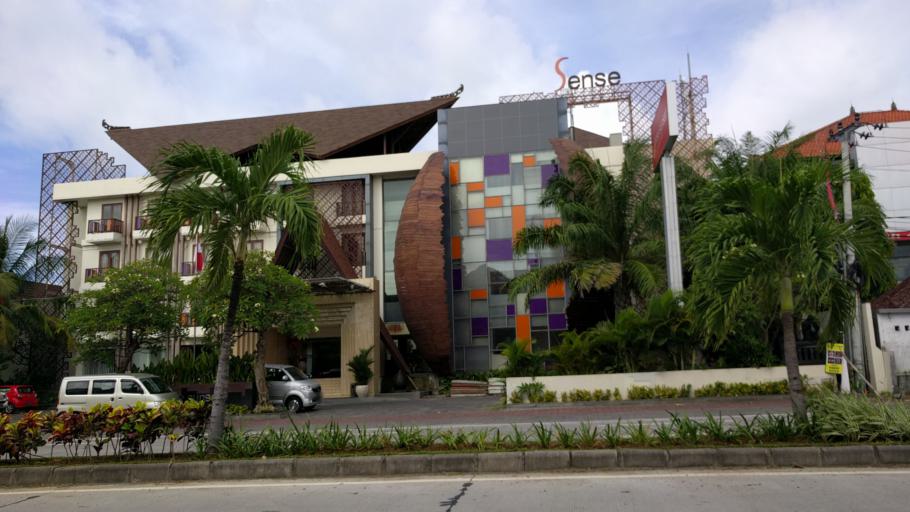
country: ID
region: Bali
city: Kuta
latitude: -8.6879
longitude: 115.1715
